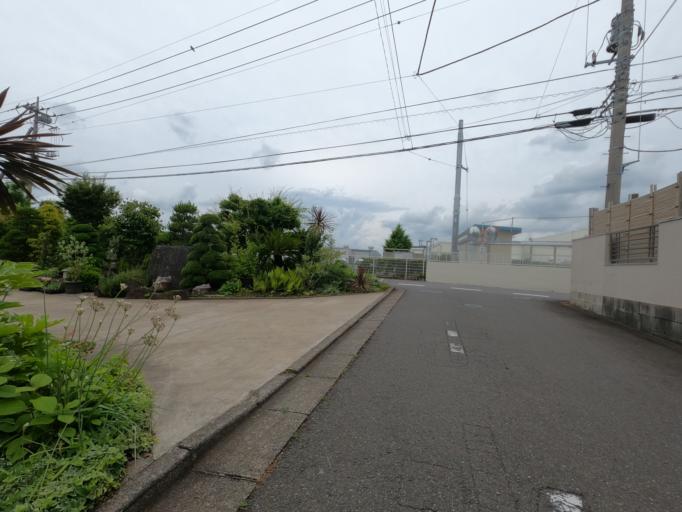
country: JP
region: Ibaraki
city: Moriya
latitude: 35.9564
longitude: 139.9852
